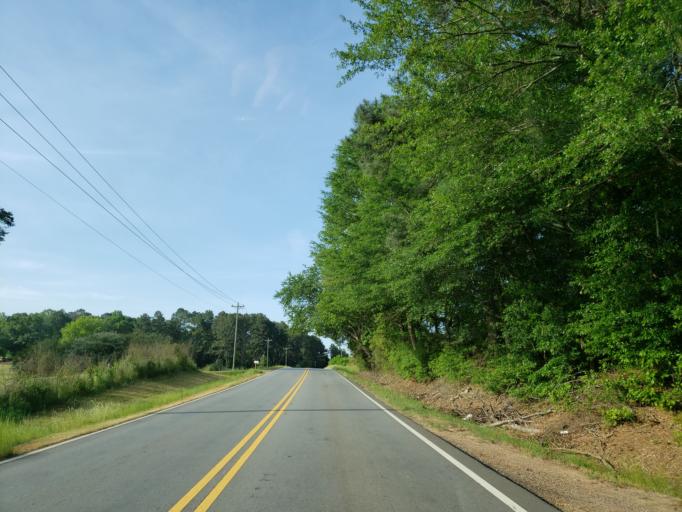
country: US
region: Georgia
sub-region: Carroll County
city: Bowdon
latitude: 33.4807
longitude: -85.2871
